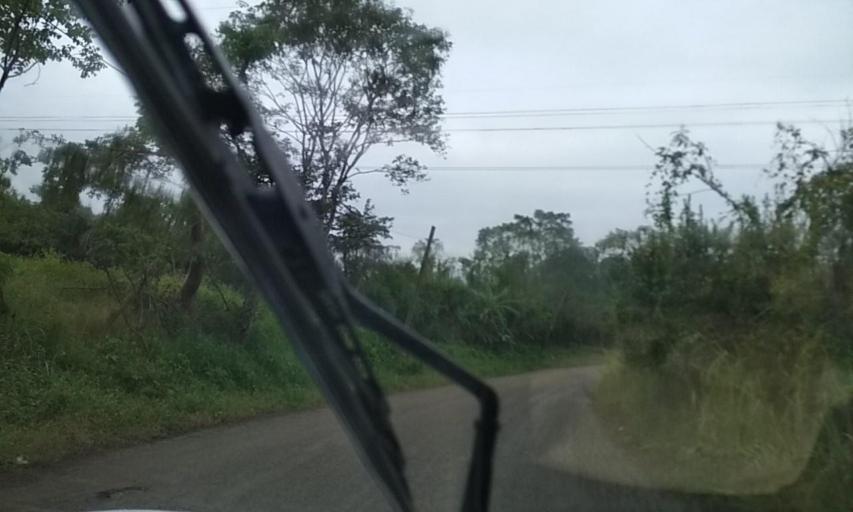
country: MX
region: Veracruz
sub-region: Coatzintla
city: Manuel Maria Contreras
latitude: 20.4494
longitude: -97.4776
